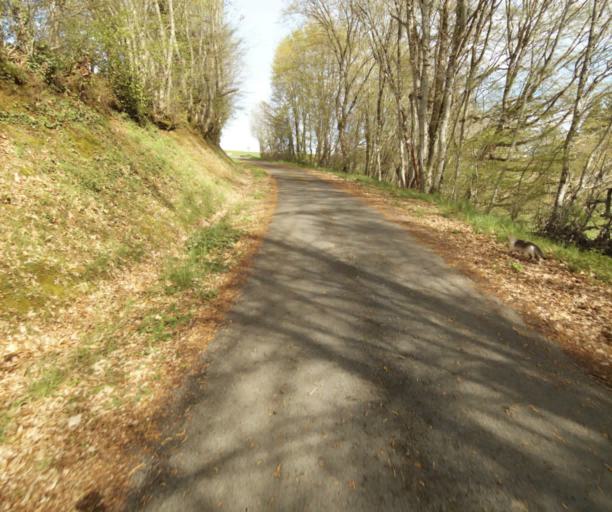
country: FR
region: Limousin
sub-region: Departement de la Correze
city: Laguenne
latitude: 45.2693
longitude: 1.8111
